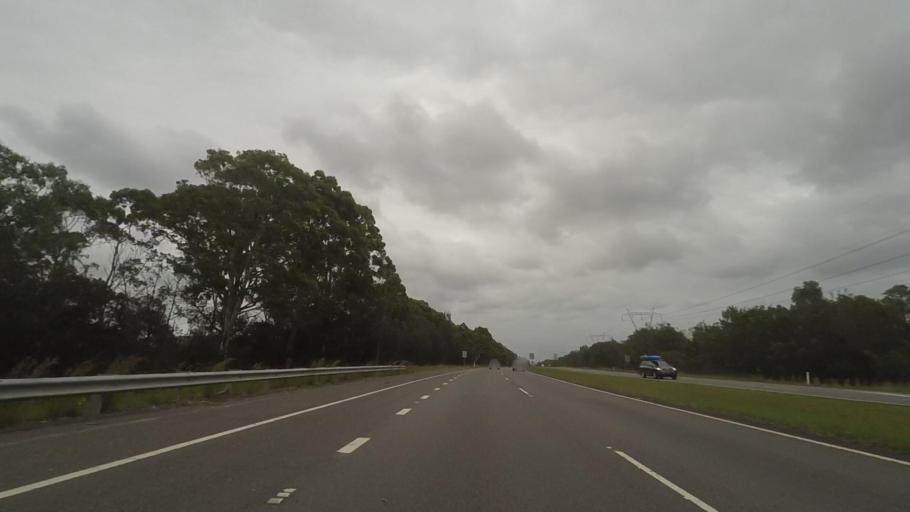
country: AU
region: New South Wales
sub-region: Wyong Shire
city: Charmhaven
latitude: -33.2061
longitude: 151.5139
